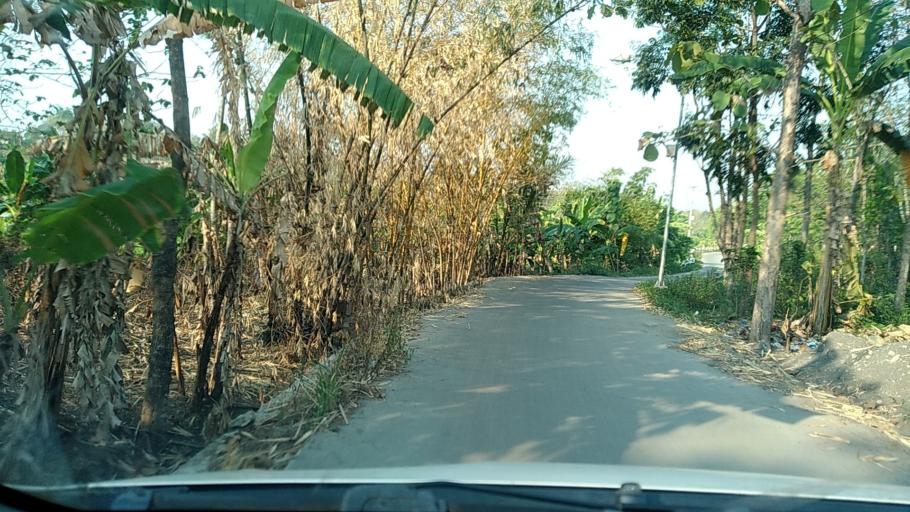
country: ID
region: Central Java
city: Mranggen
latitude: -7.0703
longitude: 110.4620
